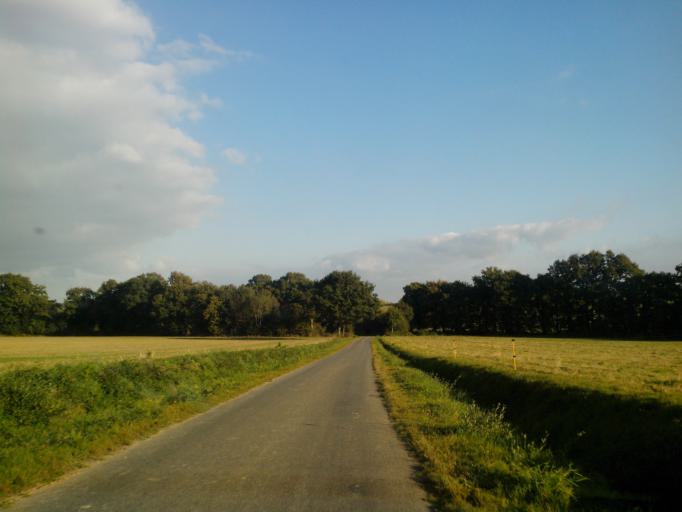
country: FR
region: Brittany
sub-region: Departement du Morbihan
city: Guilliers
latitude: 48.1124
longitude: -2.3684
